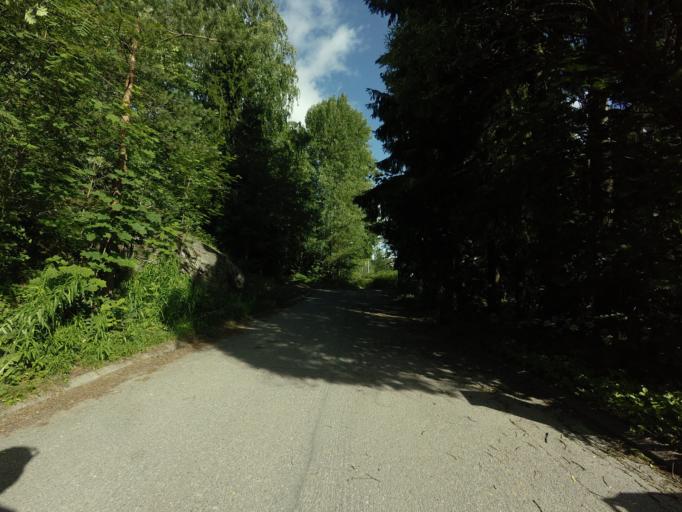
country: FI
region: Uusimaa
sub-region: Helsinki
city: Espoo
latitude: 60.1714
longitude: 24.6932
